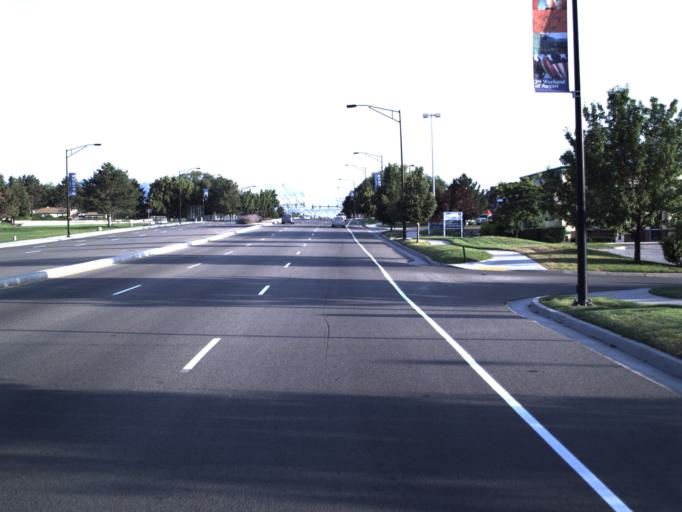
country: US
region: Utah
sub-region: Salt Lake County
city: Sandy City
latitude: 40.5692
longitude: -111.8909
